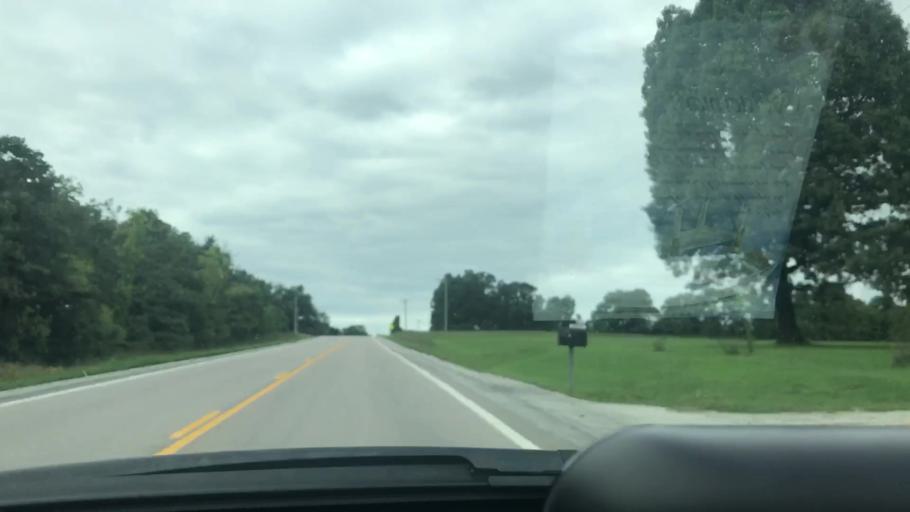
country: US
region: Missouri
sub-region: Benton County
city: Warsaw
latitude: 38.1517
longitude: -93.2946
